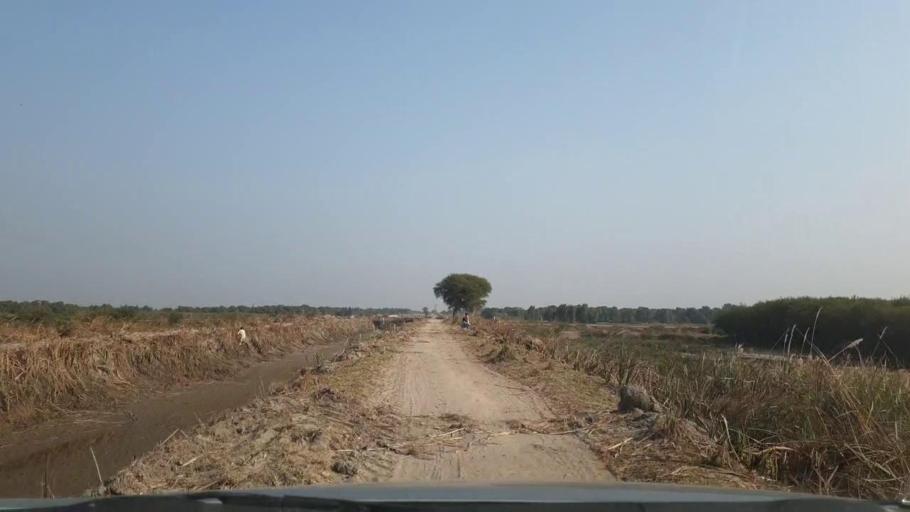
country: PK
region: Sindh
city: Tando Adam
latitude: 25.6447
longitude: 68.6029
